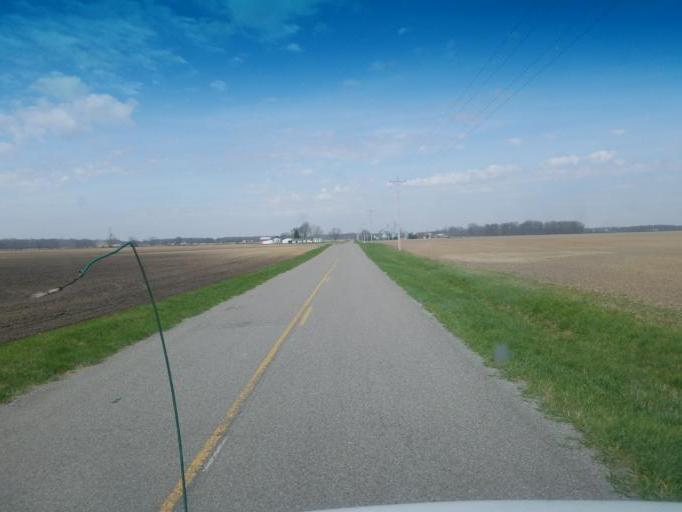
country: US
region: Ohio
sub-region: Logan County
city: Northwood
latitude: 40.4955
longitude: -83.5978
